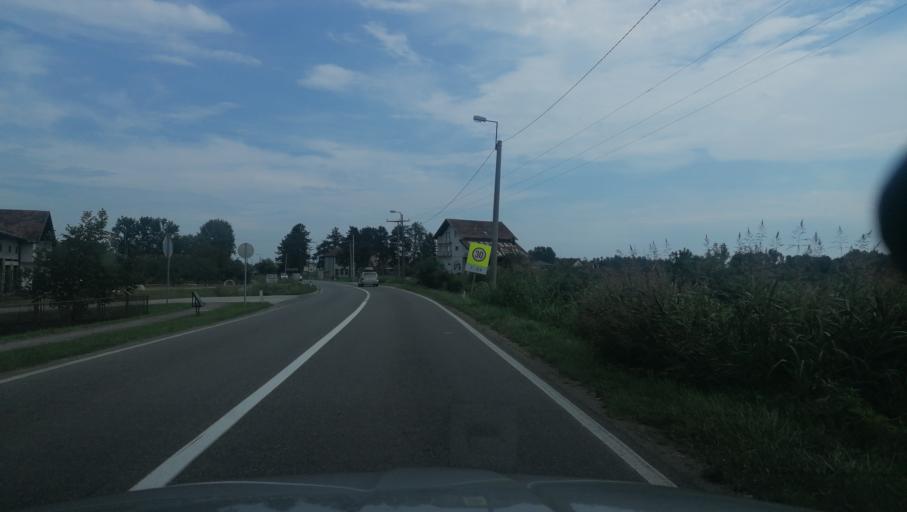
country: BA
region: Brcko
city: Brka
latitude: 44.9283
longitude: 18.7144
